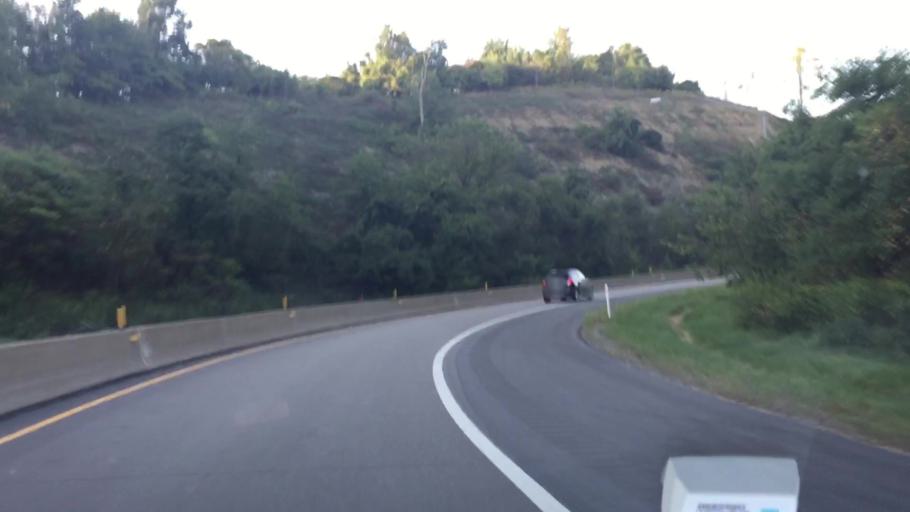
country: US
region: Pennsylvania
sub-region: Beaver County
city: Ambridge
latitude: 40.5599
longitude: -80.2819
